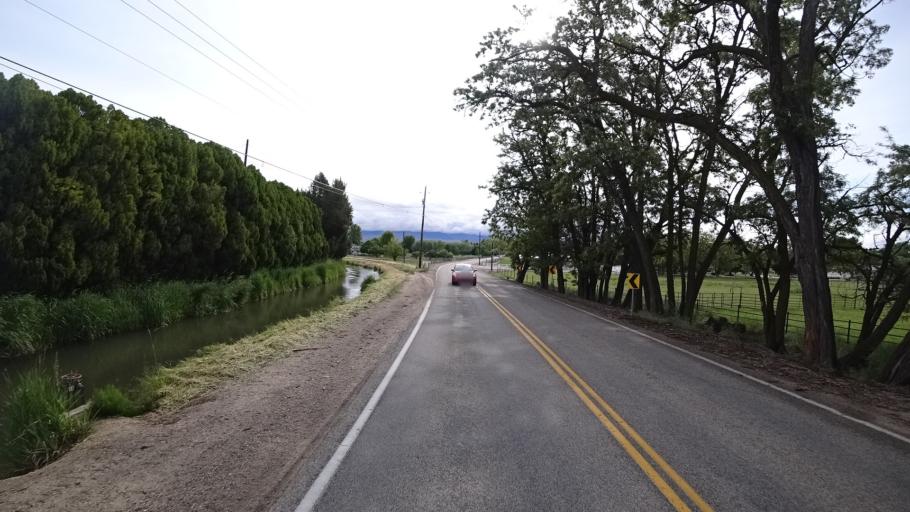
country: US
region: Idaho
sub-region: Ada County
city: Eagle
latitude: 43.7207
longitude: -116.3353
